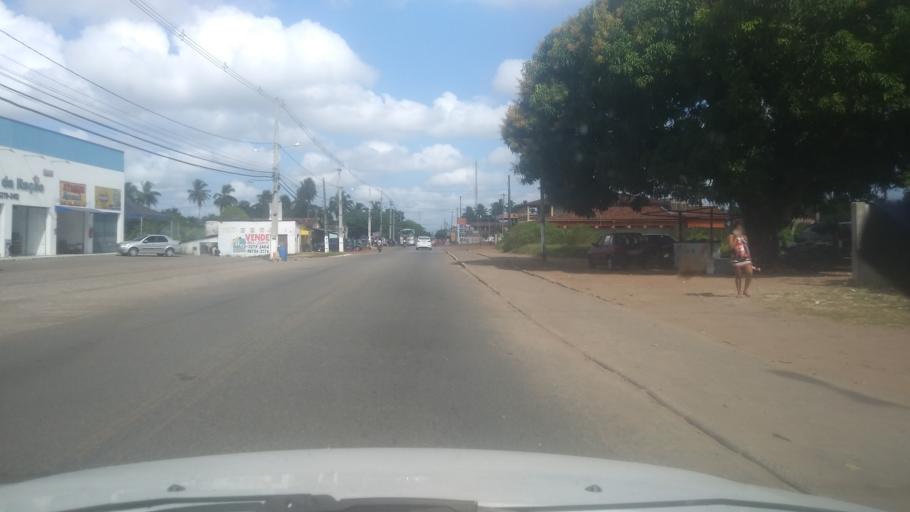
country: BR
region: Rio Grande do Norte
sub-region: Extremoz
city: Extremoz
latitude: -5.7058
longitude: -35.2988
